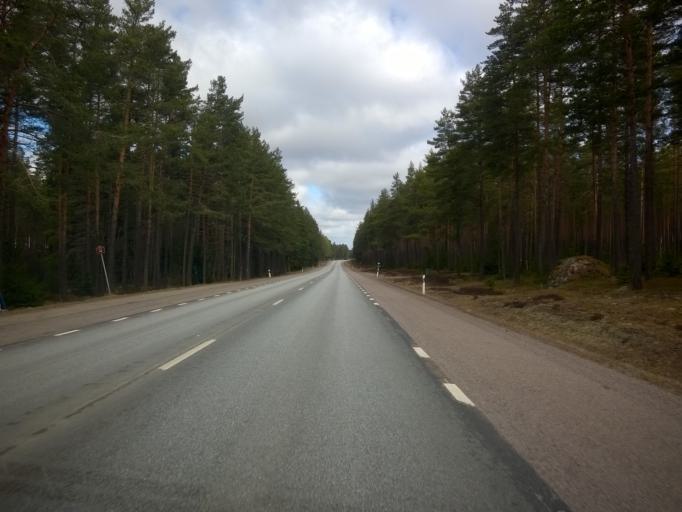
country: SE
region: Uppsala
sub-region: Tierps Kommun
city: Tierp
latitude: 60.1907
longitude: 17.4787
